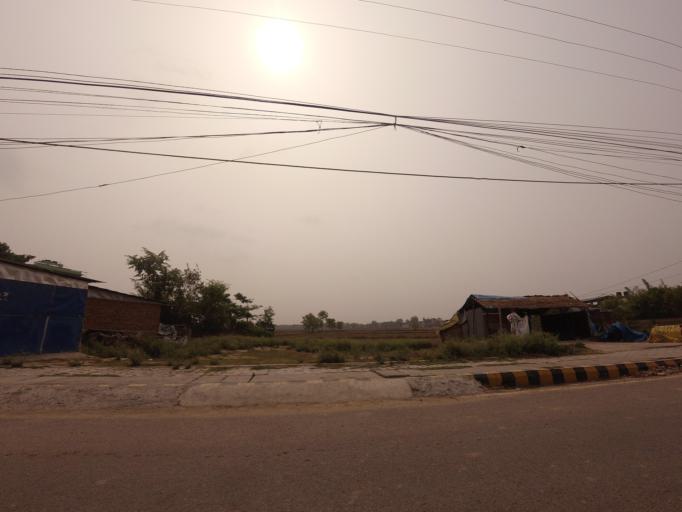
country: IN
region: Uttar Pradesh
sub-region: Maharajganj
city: Nautanwa
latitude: 27.4741
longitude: 83.2840
